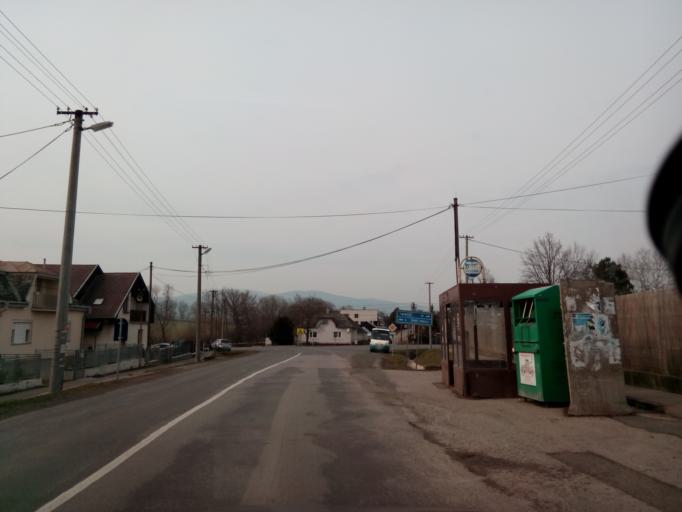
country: SK
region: Kosicky
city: Trebisov
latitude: 48.6068
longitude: 21.6244
